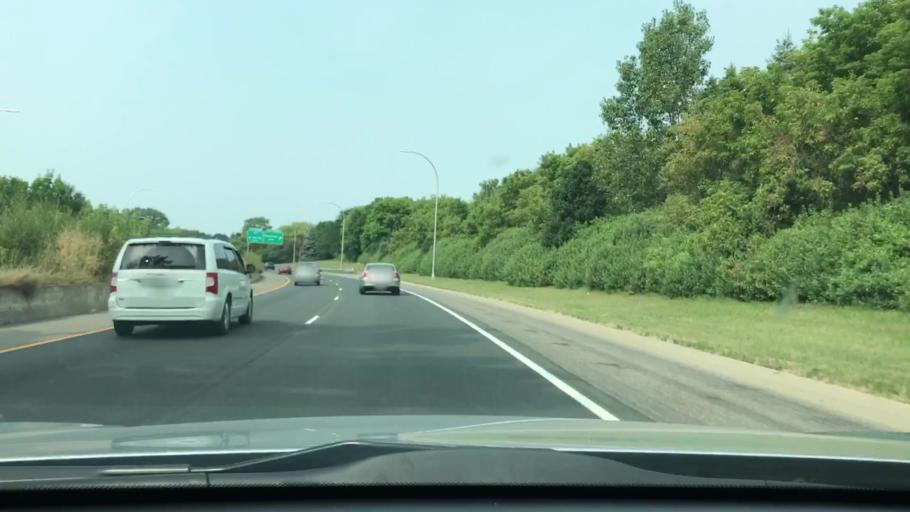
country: US
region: Minnesota
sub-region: Dakota County
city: West Saint Paul
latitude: 44.9316
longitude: -93.1379
